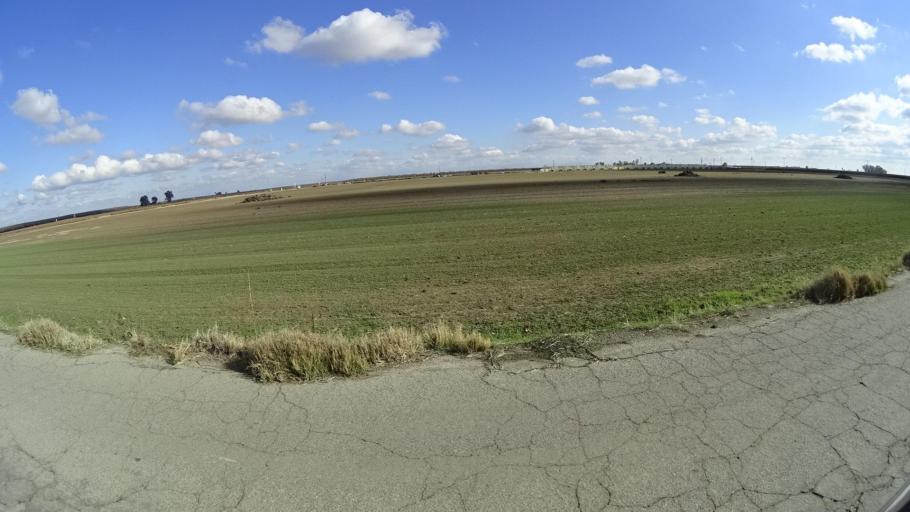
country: US
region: California
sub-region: Kern County
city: Delano
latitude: 35.7420
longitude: -119.3487
